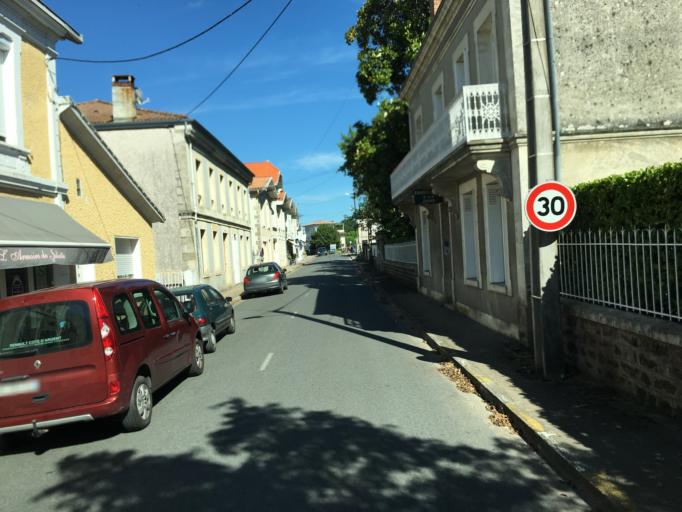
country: FR
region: Aquitaine
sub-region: Departement de la Gironde
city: Belin-Beliet
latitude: 44.5082
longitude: -0.7881
